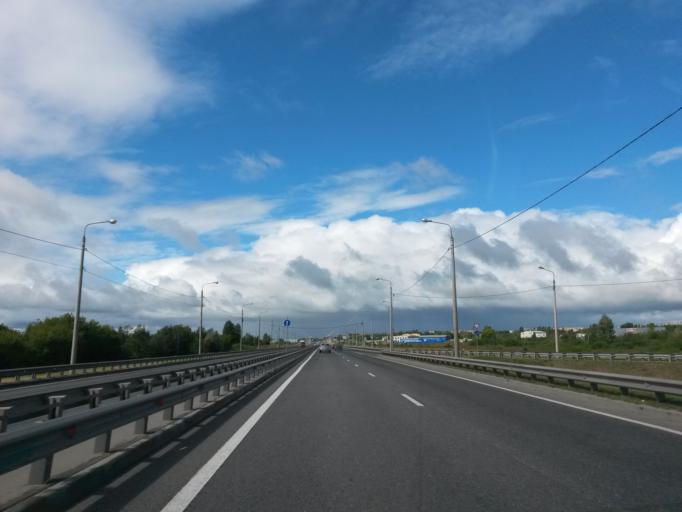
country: RU
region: Jaroslavl
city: Yaroslavl
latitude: 57.6679
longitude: 39.8134
